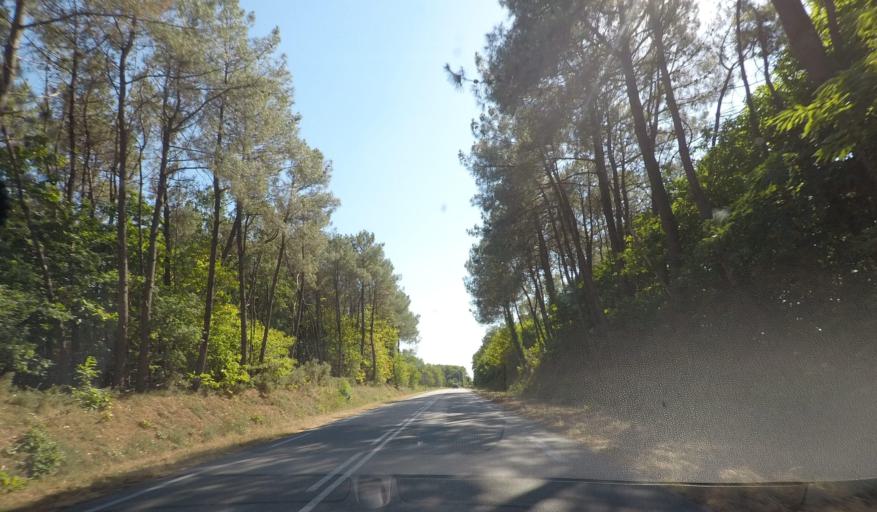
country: FR
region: Brittany
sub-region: Departement du Morbihan
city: Peaule
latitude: 47.5749
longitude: -2.3811
